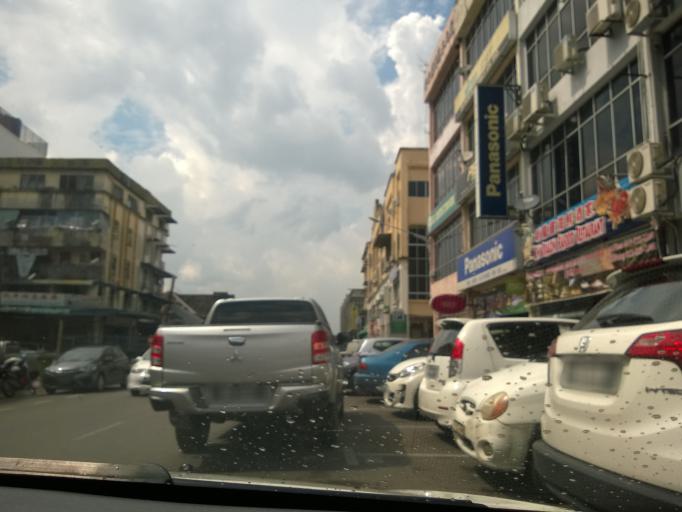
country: MY
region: Sarawak
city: Sibu
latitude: 2.2915
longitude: 111.8286
